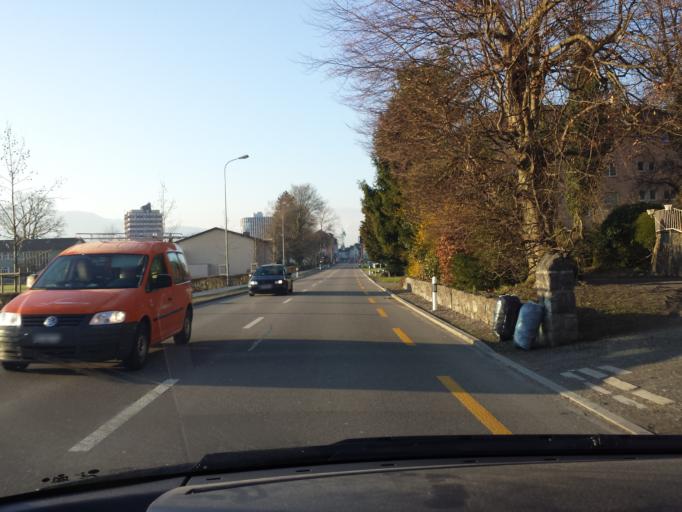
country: CH
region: Appenzell Innerrhoden
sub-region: Appenzell Inner Rhodes
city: Balgach
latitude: 47.4147
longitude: 9.6249
